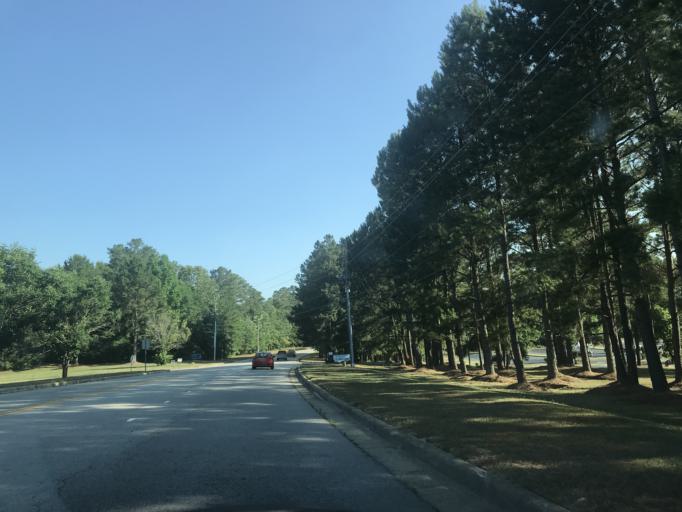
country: US
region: North Carolina
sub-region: Wake County
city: Garner
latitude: 35.7149
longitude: -78.6024
